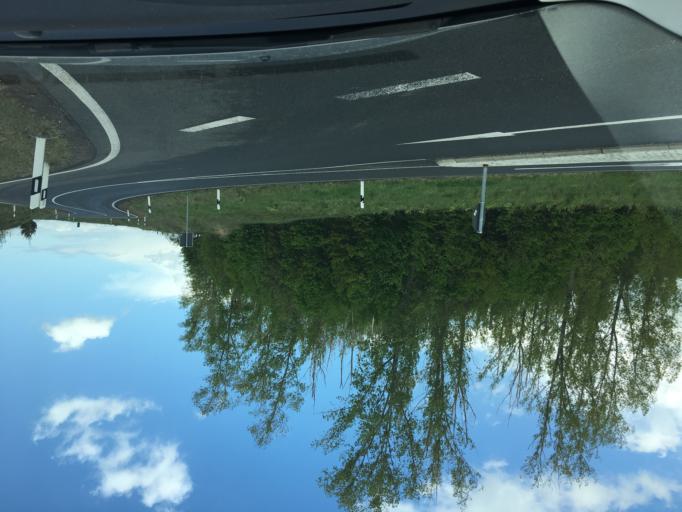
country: DE
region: Saxony
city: Borna
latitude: 51.1110
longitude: 12.5108
